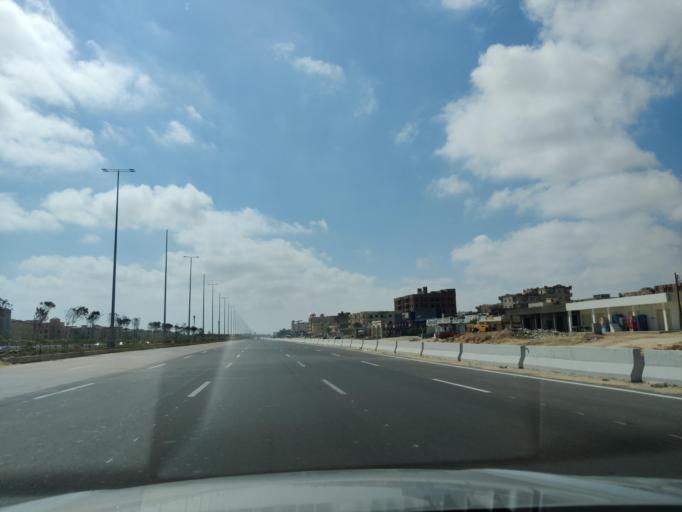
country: EG
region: Muhafazat Matruh
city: Al `Alamayn
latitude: 30.9663
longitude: 28.7473
